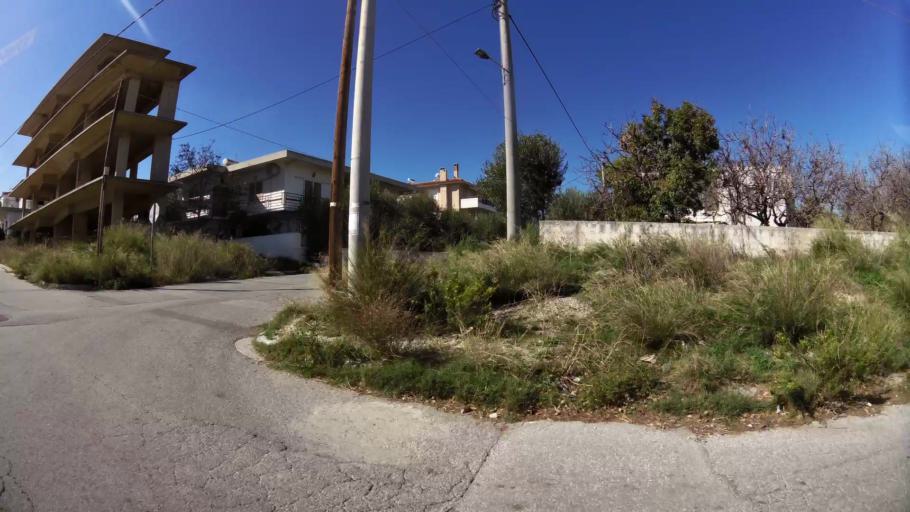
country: GR
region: Attica
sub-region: Nomarchia Anatolikis Attikis
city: Markopoulo
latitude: 37.8861
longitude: 23.9424
